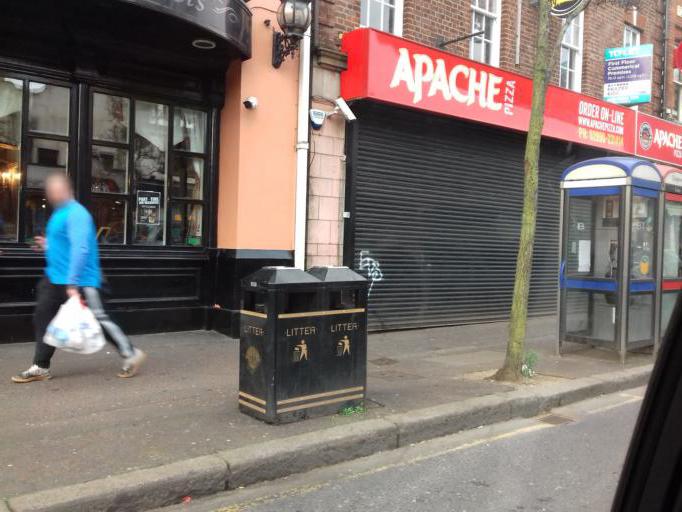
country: GB
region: Northern Ireland
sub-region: City of Belfast
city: Belfast
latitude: 54.5891
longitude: -5.9347
